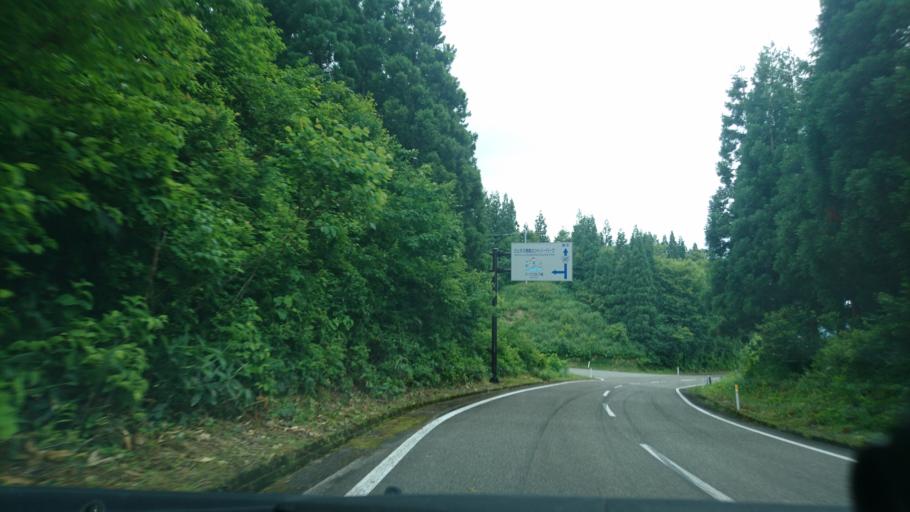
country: JP
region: Akita
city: Yuzawa
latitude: 39.1584
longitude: 140.7499
